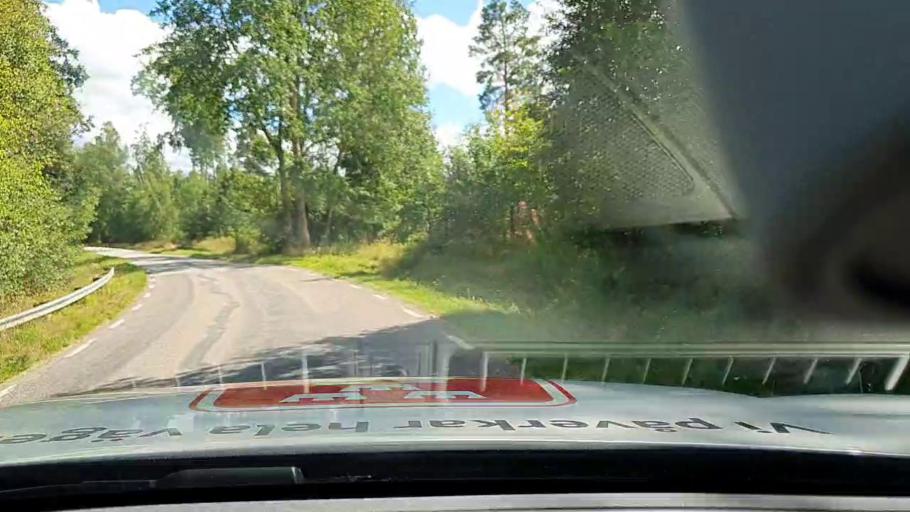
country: SE
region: Vaestra Goetaland
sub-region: Toreboda Kommun
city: Toereboda
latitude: 58.5709
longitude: 14.1277
